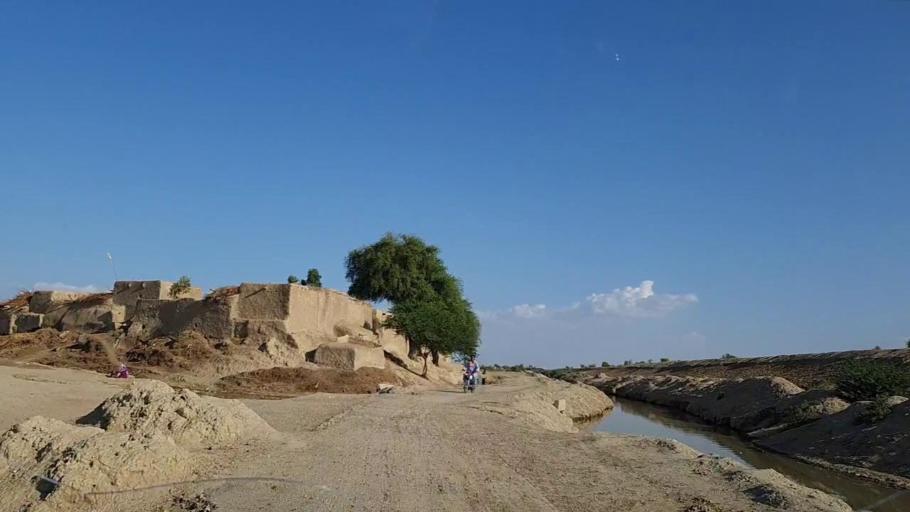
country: PK
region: Sindh
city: Johi
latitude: 26.5847
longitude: 67.5420
